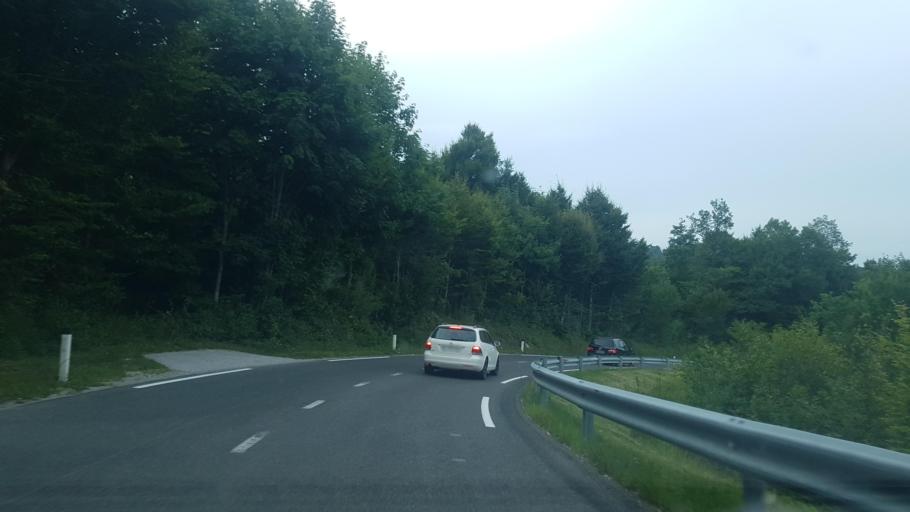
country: SI
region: Logatec
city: Logatec
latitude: 45.8942
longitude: 14.1713
